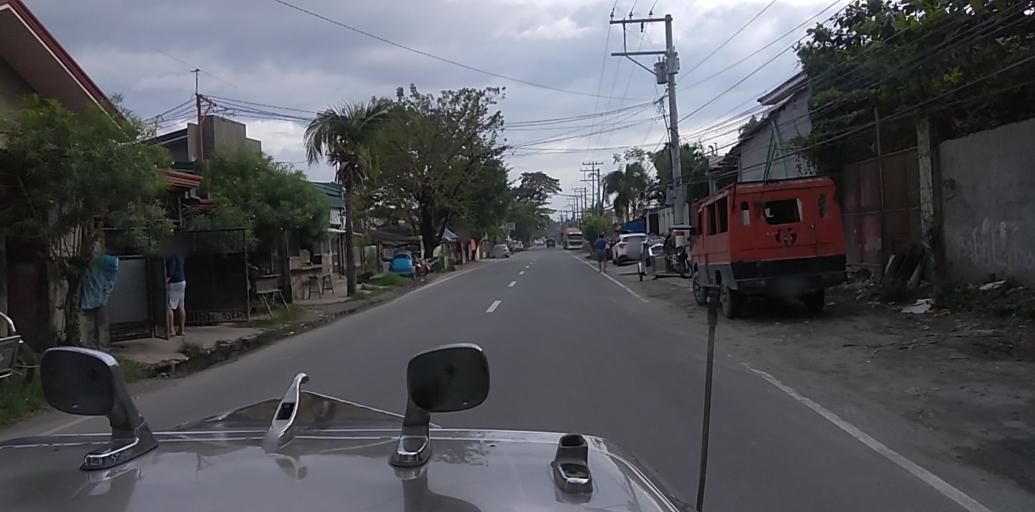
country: PH
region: Central Luzon
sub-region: Province of Pampanga
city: Minalin
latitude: 14.9940
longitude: 120.7042
